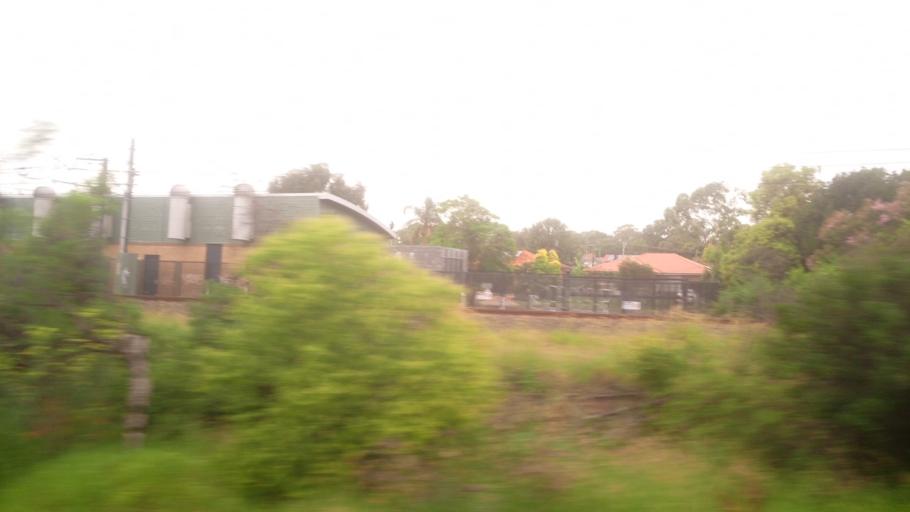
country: AU
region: New South Wales
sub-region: Blacktown
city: Blacktown
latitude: -33.7745
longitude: 150.9258
